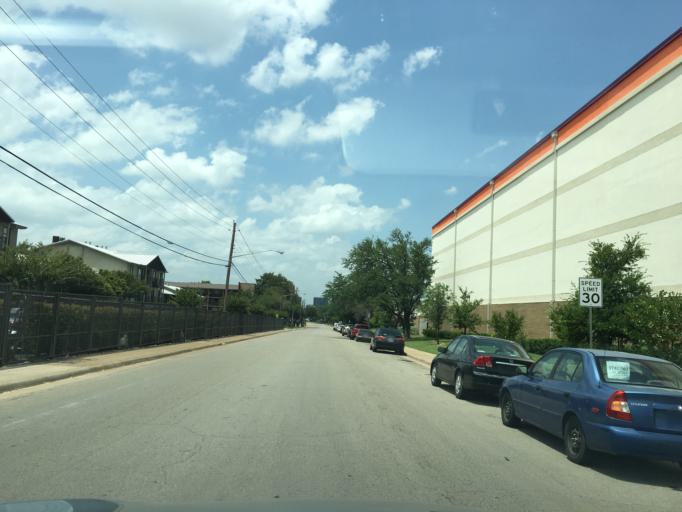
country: US
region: Texas
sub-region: Dallas County
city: University Park
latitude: 32.8901
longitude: -96.7728
